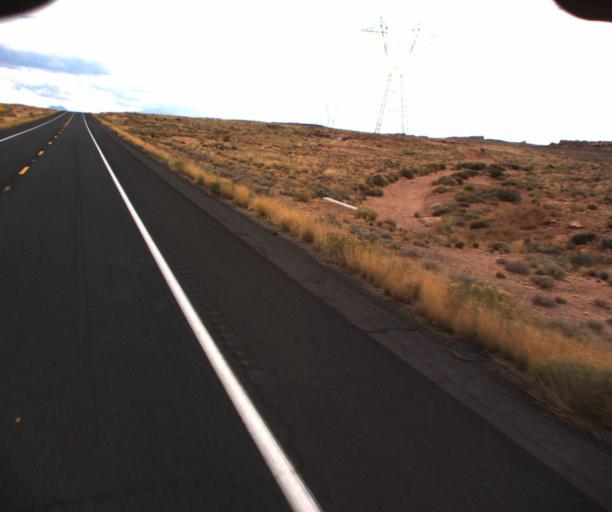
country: US
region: Arizona
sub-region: Coconino County
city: Tuba City
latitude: 35.8173
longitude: -111.4417
